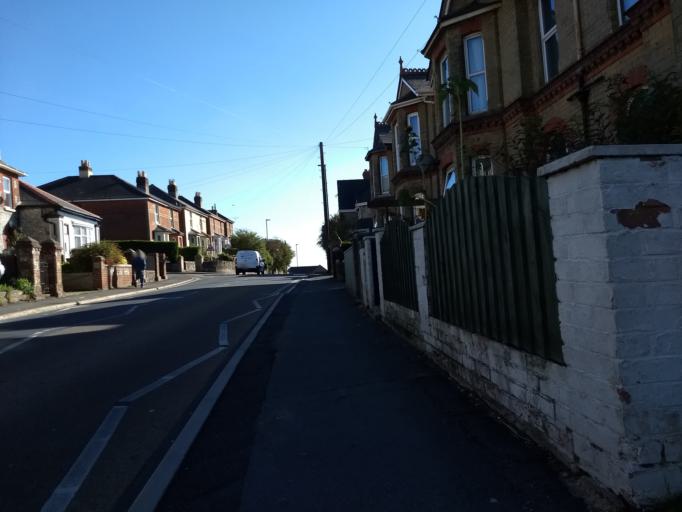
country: GB
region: England
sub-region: Isle of Wight
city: Ventnor
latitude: 50.5976
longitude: -1.2155
